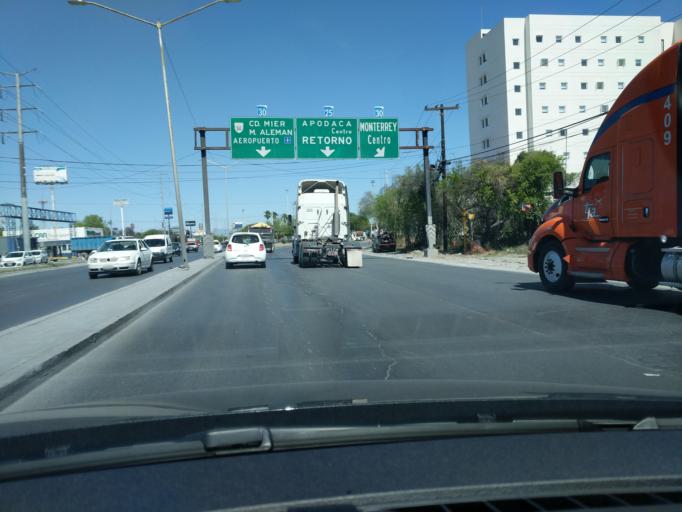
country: MX
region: Nuevo Leon
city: Apodaca
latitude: 25.7739
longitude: -100.1897
